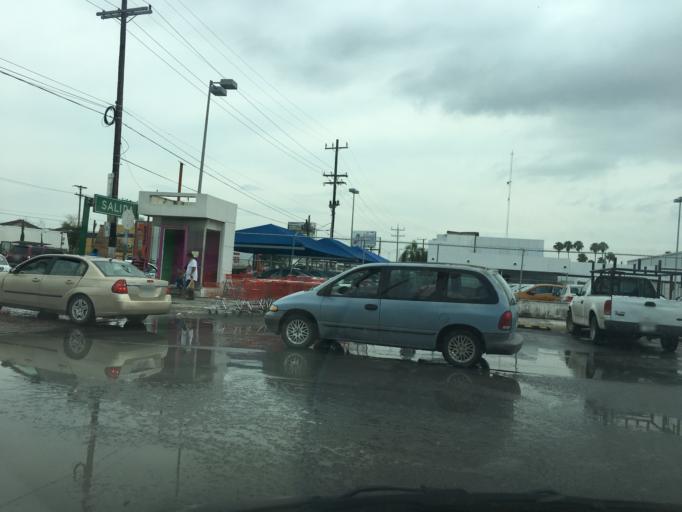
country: MX
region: Tamaulipas
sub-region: Matamoros
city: Heroica Matamoros
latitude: 25.8769
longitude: -97.5216
